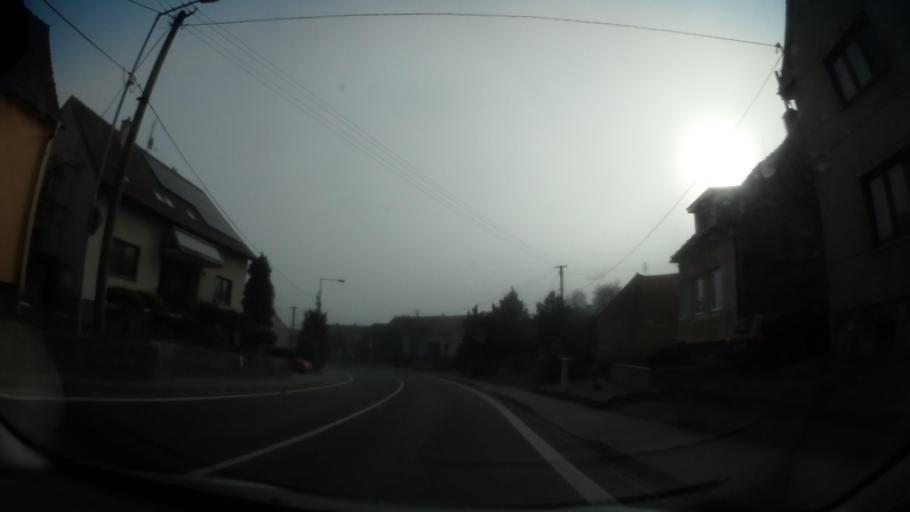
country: CZ
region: South Moravian
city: Zdanice
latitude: 49.0435
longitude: 17.0001
